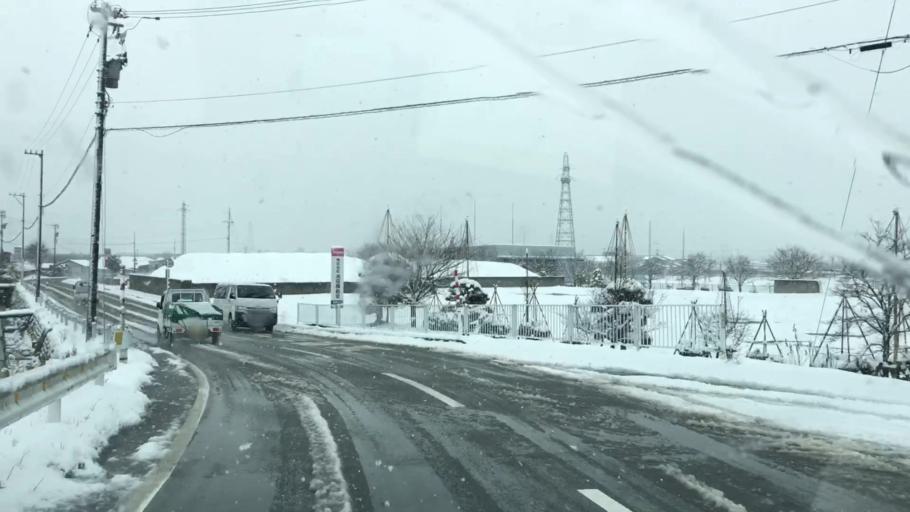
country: JP
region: Toyama
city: Kamiichi
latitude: 36.6972
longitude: 137.3380
